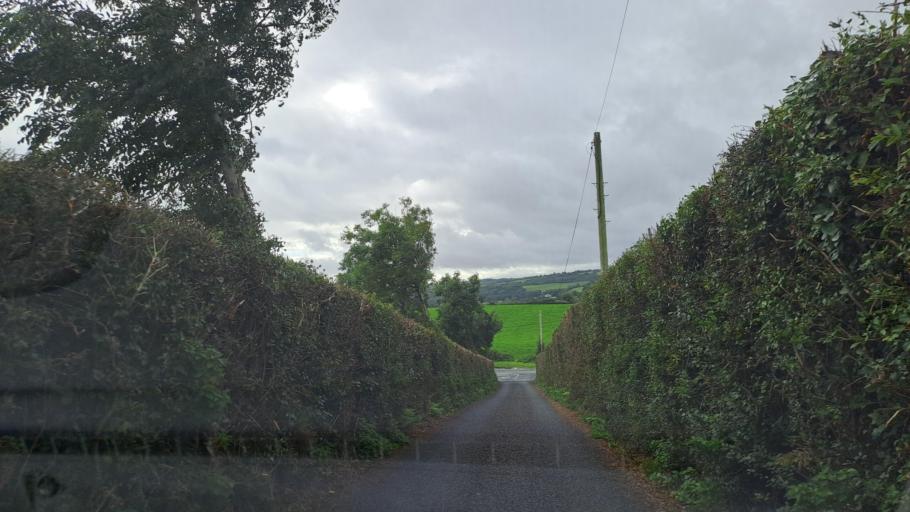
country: IE
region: Ulster
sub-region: County Monaghan
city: Carrickmacross
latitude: 53.9605
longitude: -6.7744
